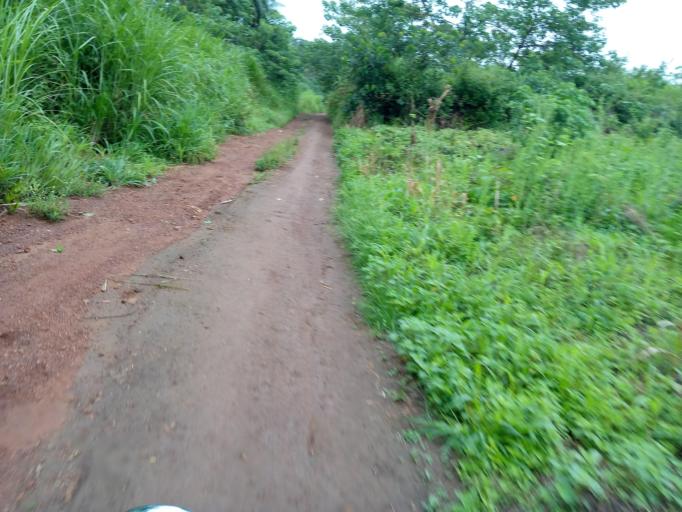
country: SL
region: Eastern Province
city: Buedu
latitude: 8.4689
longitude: -10.3453
